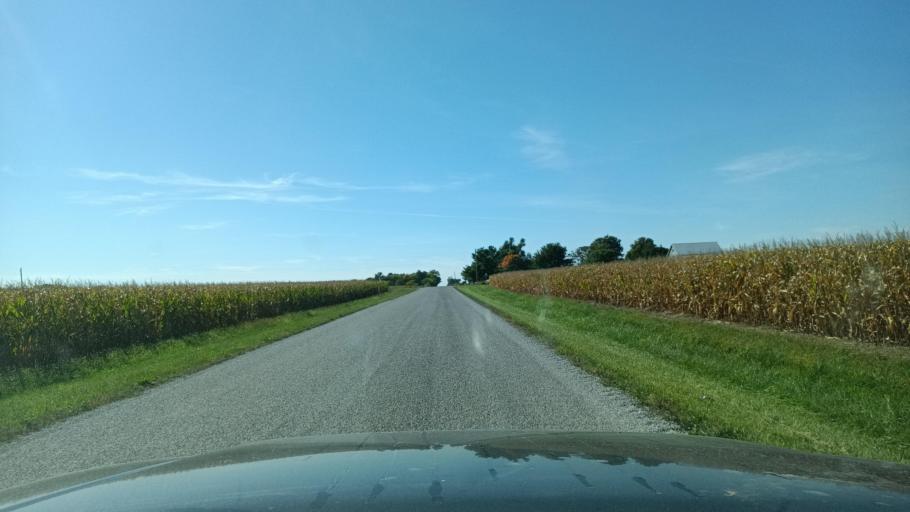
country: US
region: Illinois
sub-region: Logan County
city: Atlanta
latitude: 40.2436
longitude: -89.1889
